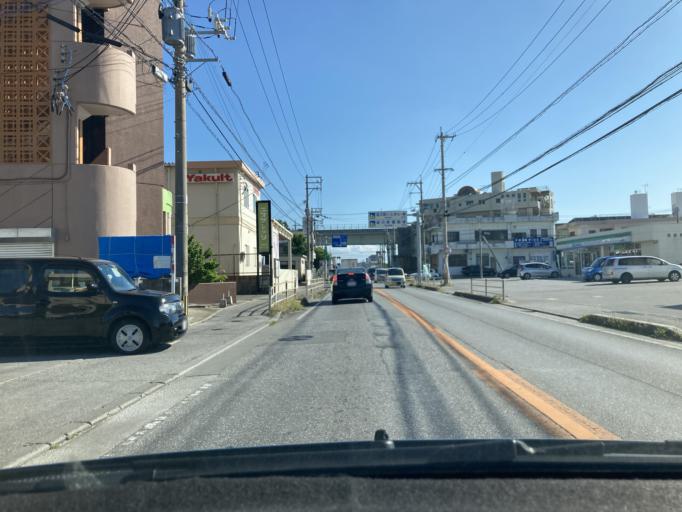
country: JP
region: Okinawa
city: Tomigusuku
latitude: 26.1765
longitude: 127.6654
